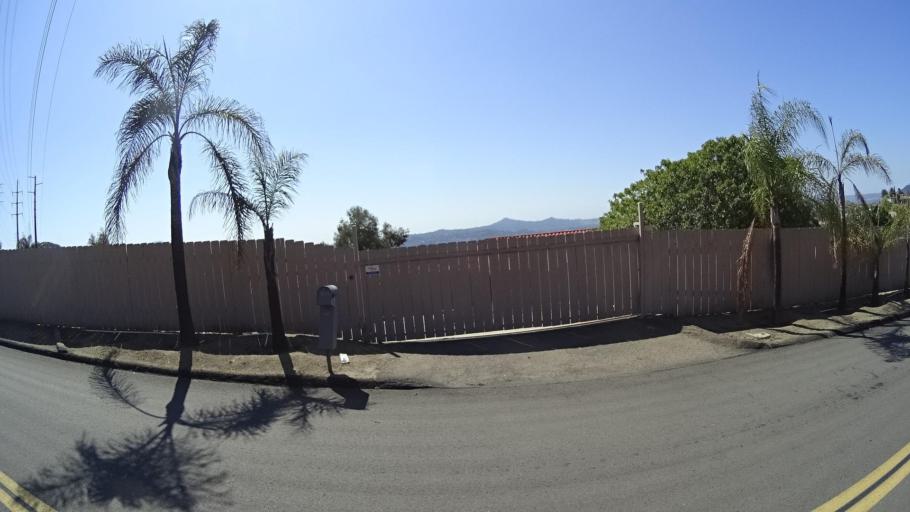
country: US
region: California
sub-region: San Diego County
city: Granite Hills
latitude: 32.8029
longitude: -116.8928
